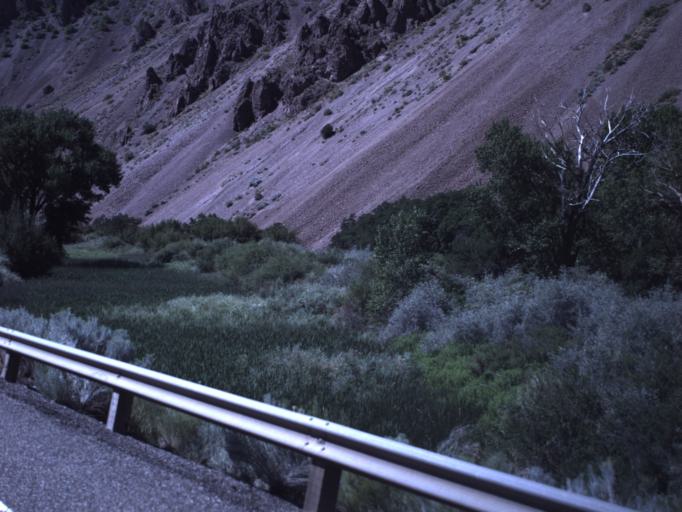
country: US
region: Utah
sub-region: Sevier County
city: Monroe
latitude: 38.5014
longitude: -112.2578
